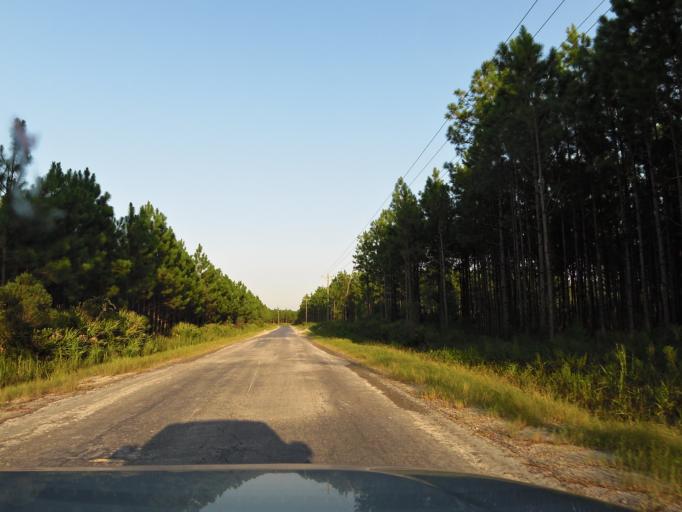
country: US
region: Florida
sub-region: Baker County
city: Macclenny
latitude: 30.3928
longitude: -82.0939
